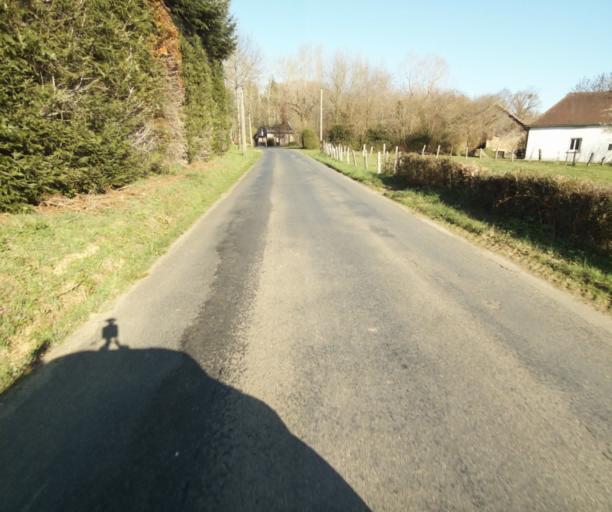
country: FR
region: Limousin
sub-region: Departement de la Correze
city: Saint-Clement
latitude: 45.3416
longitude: 1.6783
